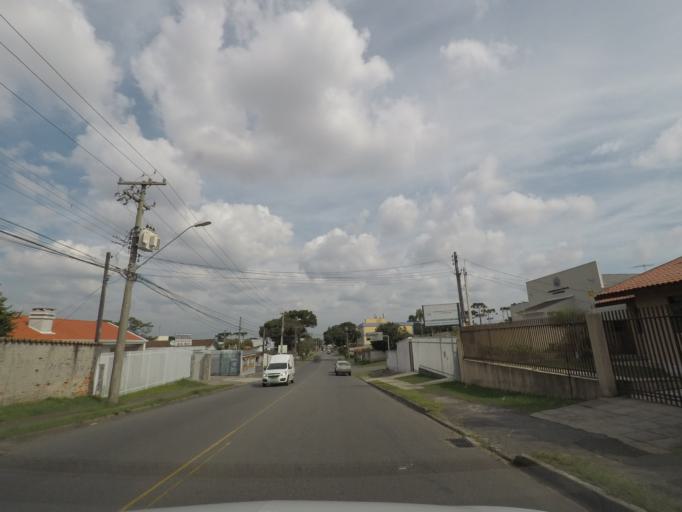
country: BR
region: Parana
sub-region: Sao Jose Dos Pinhais
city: Sao Jose dos Pinhais
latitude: -25.4892
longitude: -49.2143
